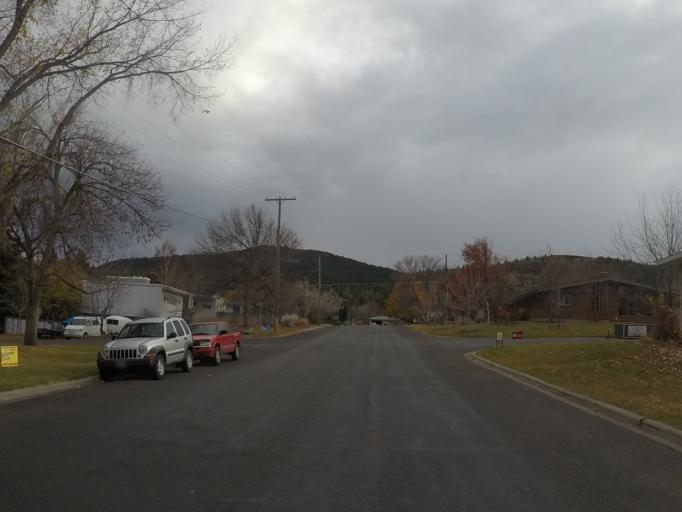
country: US
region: Montana
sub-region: Lewis and Clark County
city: Helena
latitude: 46.5835
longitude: -112.0147
